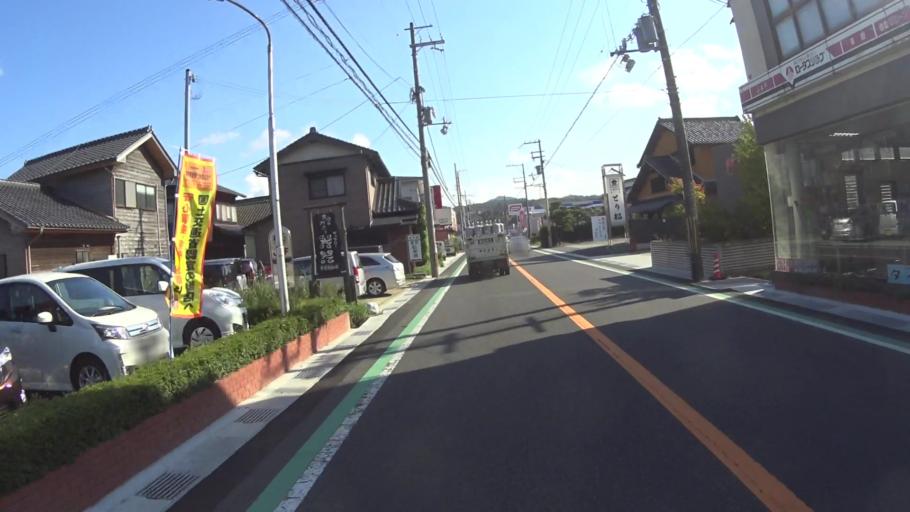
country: JP
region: Kyoto
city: Miyazu
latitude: 35.6737
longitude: 135.0280
